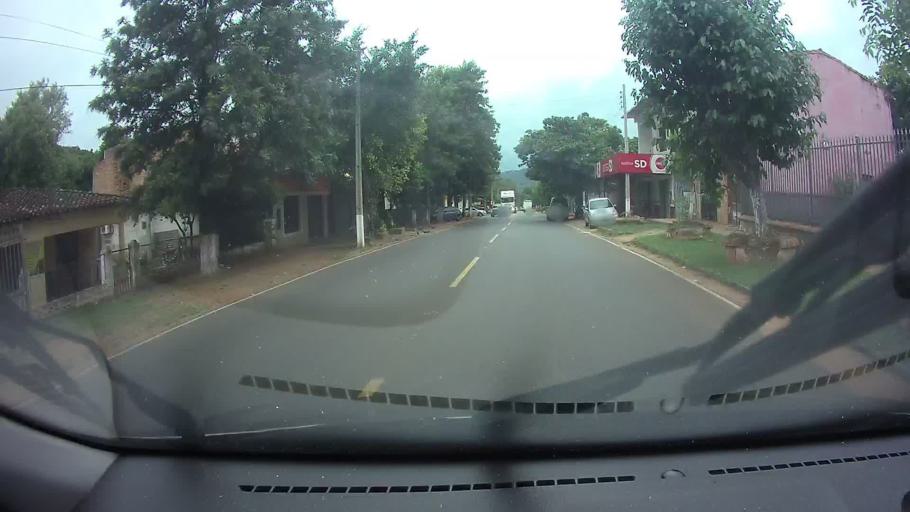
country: PY
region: Paraguari
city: Carapegua
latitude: -25.7655
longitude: -57.2482
